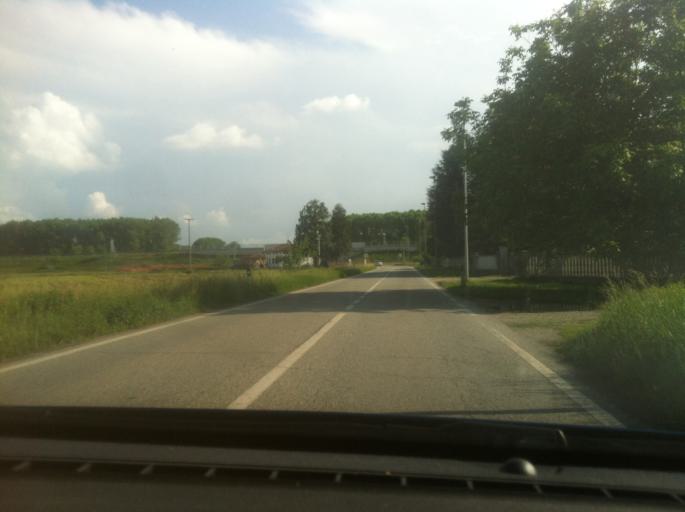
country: IT
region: Piedmont
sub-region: Provincia di Torino
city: Pavone Canavese
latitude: 45.4269
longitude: 7.8589
